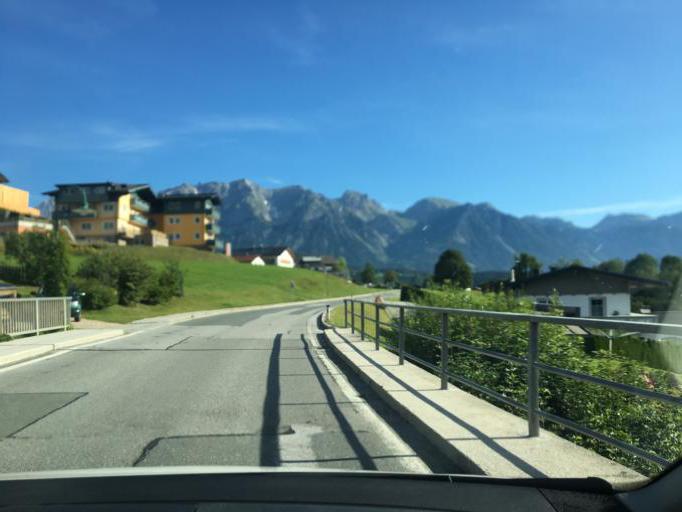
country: AT
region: Styria
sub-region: Politischer Bezirk Liezen
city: Schladming
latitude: 47.3796
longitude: 13.6723
